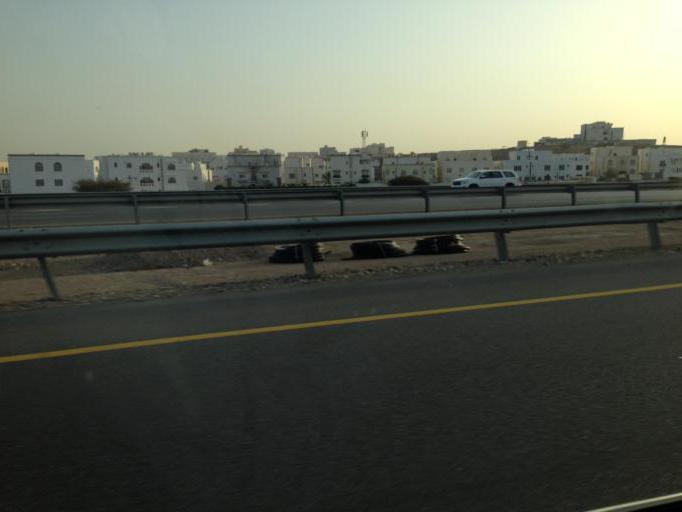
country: OM
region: Muhafazat Masqat
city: Bawshar
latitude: 23.5642
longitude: 58.3856
